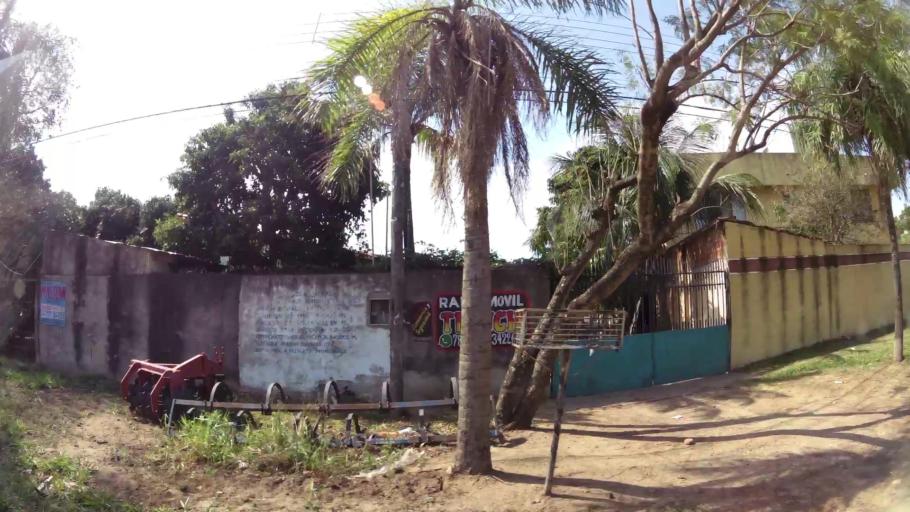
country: BO
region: Santa Cruz
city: Santa Cruz de la Sierra
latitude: -17.7505
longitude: -63.1600
